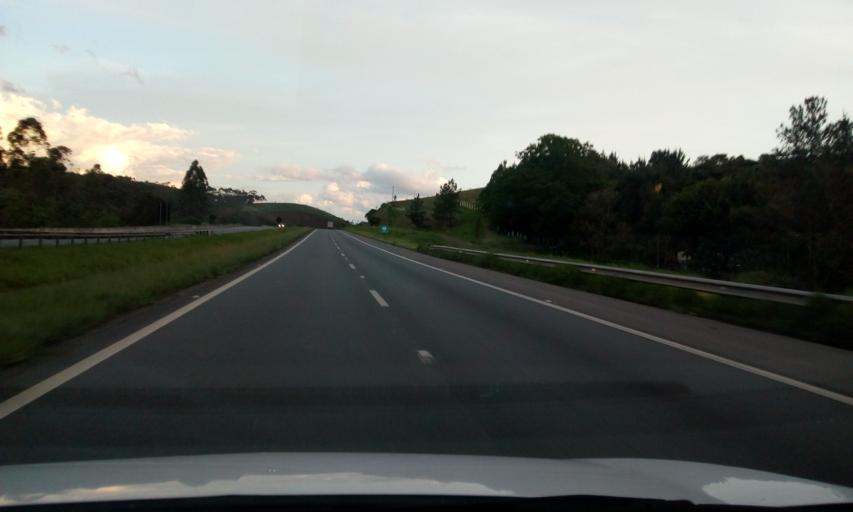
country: BR
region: Sao Paulo
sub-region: Santa Isabel
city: Santa Isabel
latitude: -23.1707
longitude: -46.2194
